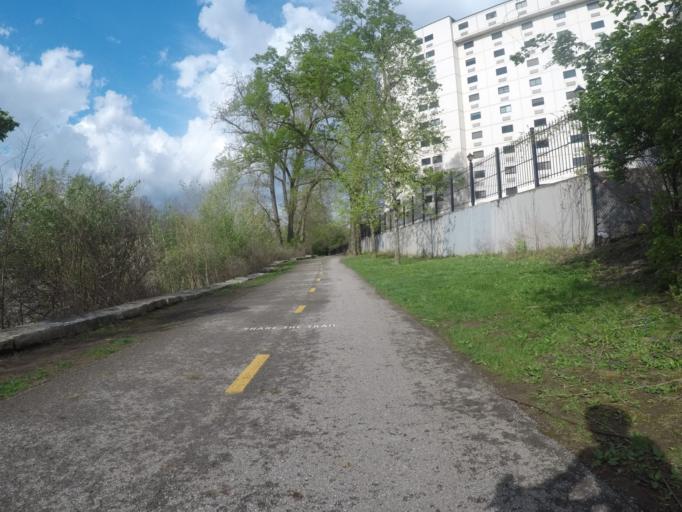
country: US
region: Ohio
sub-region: Franklin County
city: Grandview Heights
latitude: 40.0074
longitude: -83.0204
